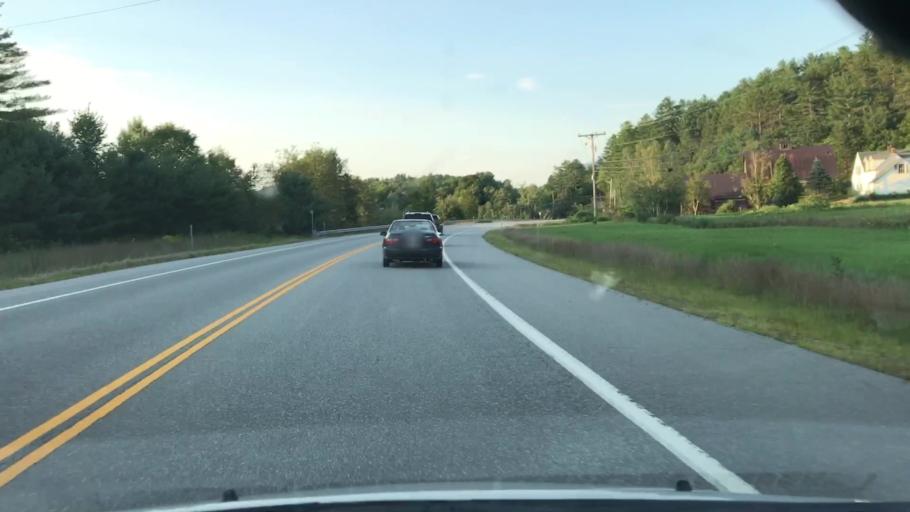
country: US
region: New Hampshire
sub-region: Grafton County
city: Rumney
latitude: 43.8608
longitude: -71.9115
